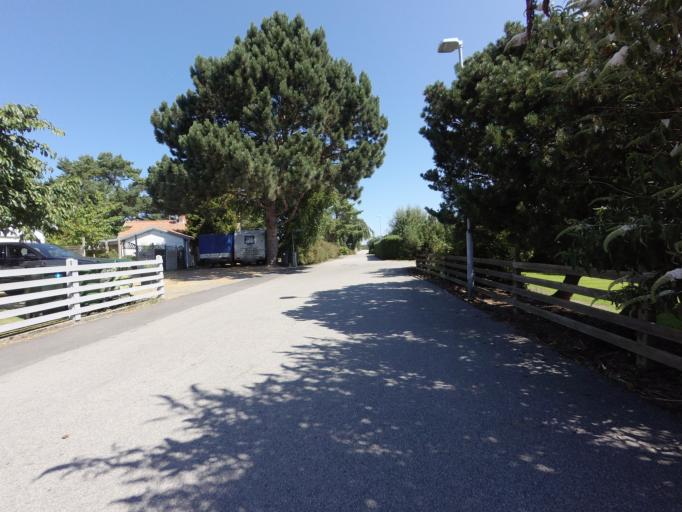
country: SE
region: Skane
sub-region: Vellinge Kommun
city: Skanor med Falsterbo
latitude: 55.3984
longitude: 12.8404
